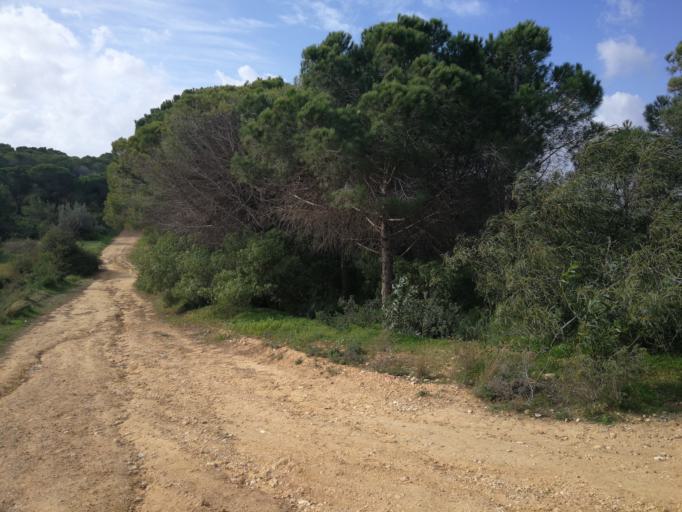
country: TN
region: Tunis
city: Al Marsa
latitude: 36.9004
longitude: 10.2982
